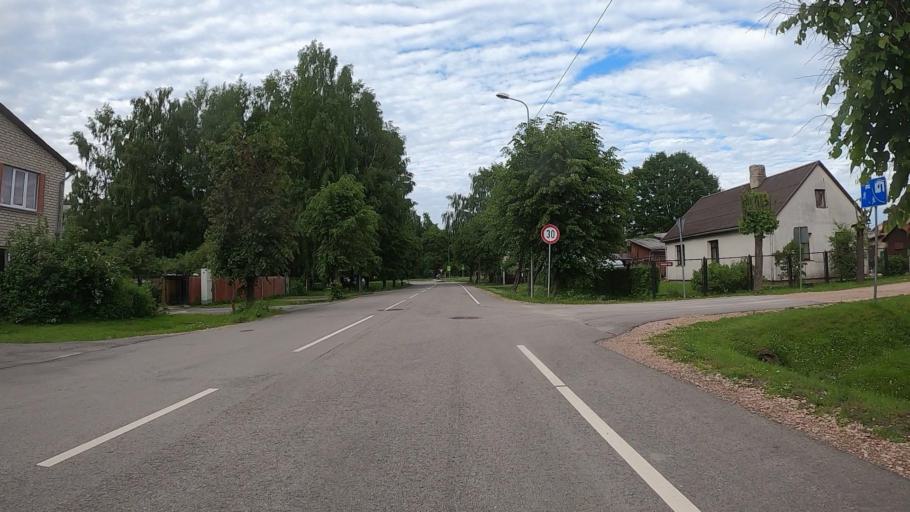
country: LV
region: Ozolnieku
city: Ozolnieki
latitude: 56.6678
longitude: 23.7506
